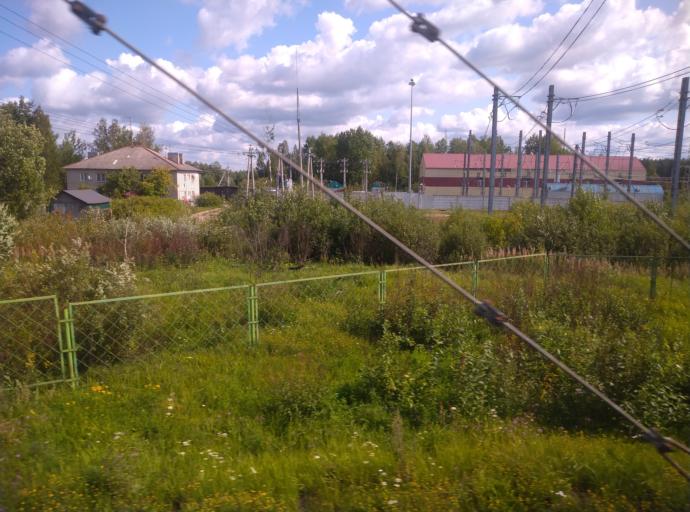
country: RU
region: Leningrad
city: Krasnyy Bor
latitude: 59.6769
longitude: 30.7060
